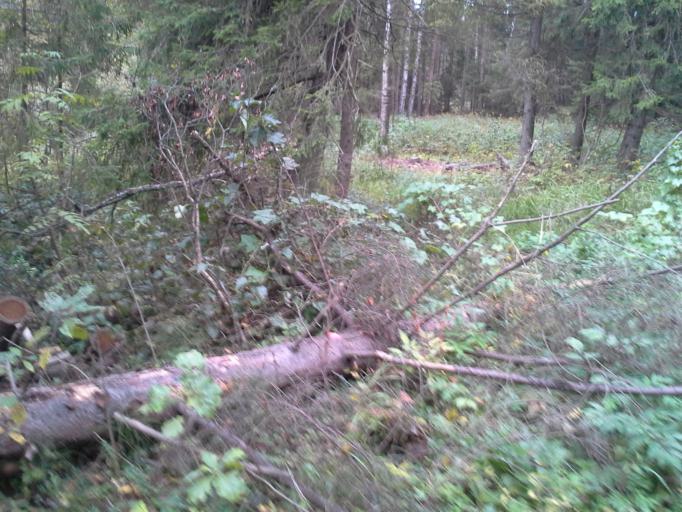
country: RU
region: Moskovskaya
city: Krasnoznamensk
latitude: 55.6224
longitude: 37.0579
